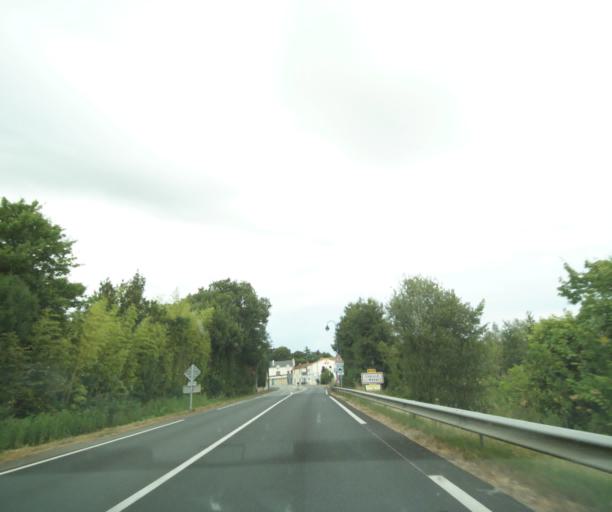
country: FR
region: Pays de la Loire
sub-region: Departement de la Vendee
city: Chaille-les-Marais
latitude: 46.3914
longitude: -1.0234
